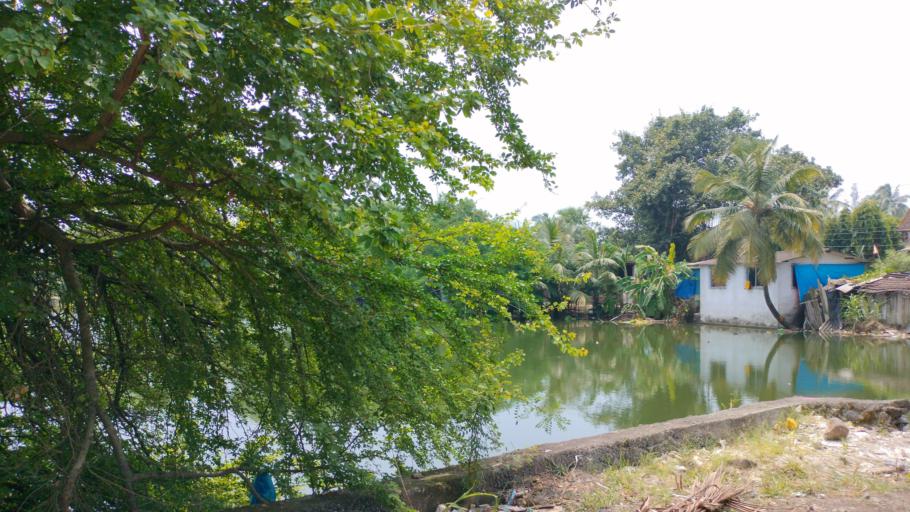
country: IN
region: Maharashtra
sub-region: Thane
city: Virar
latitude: 19.3840
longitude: 72.7763
